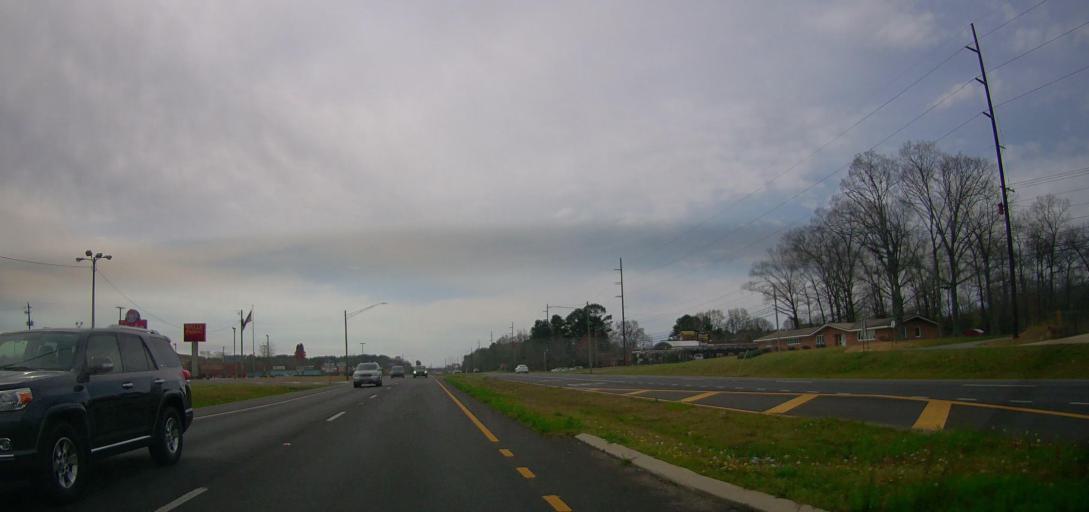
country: US
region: Alabama
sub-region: Walker County
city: Jasper
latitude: 33.8423
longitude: -87.2421
